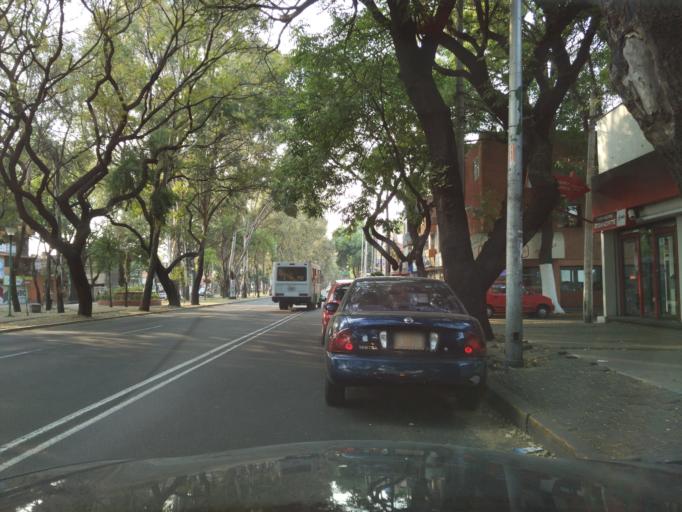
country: MX
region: Mexico City
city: Coyoacan
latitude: 19.3174
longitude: -99.1279
